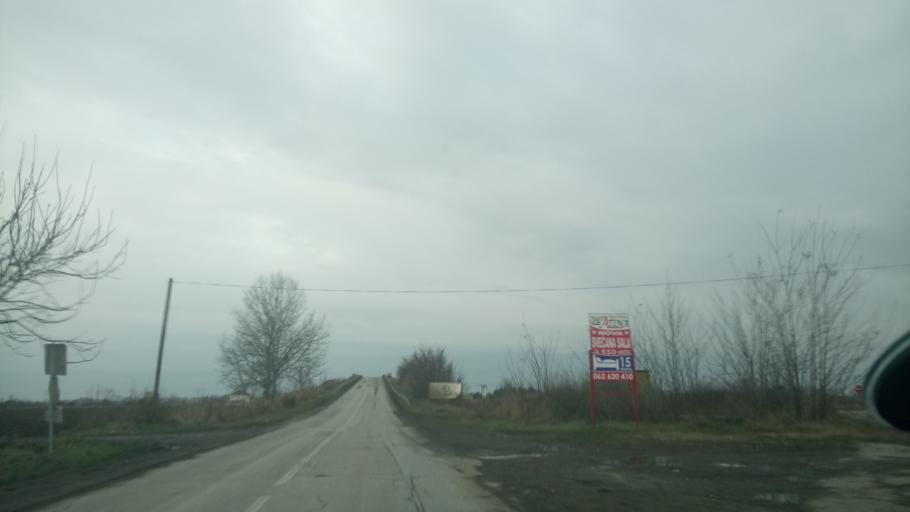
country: RS
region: Autonomna Pokrajina Vojvodina
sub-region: Sremski Okrug
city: Stara Pazova
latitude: 44.9630
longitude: 20.1603
